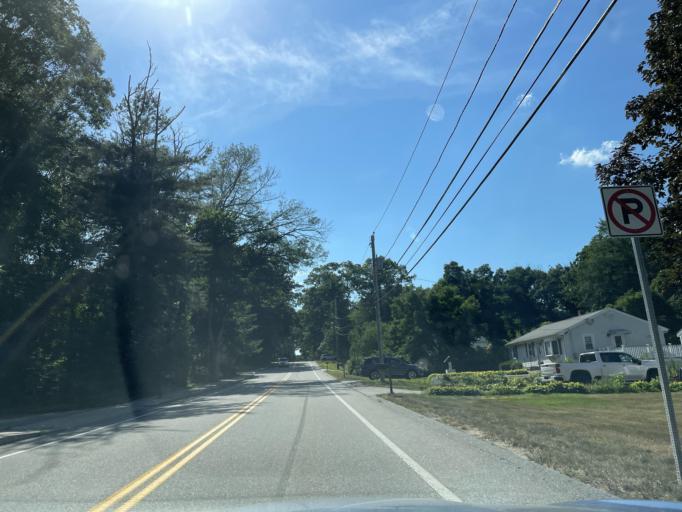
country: US
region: Massachusetts
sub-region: Worcester County
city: Northbridge
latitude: 42.1545
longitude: -71.6718
